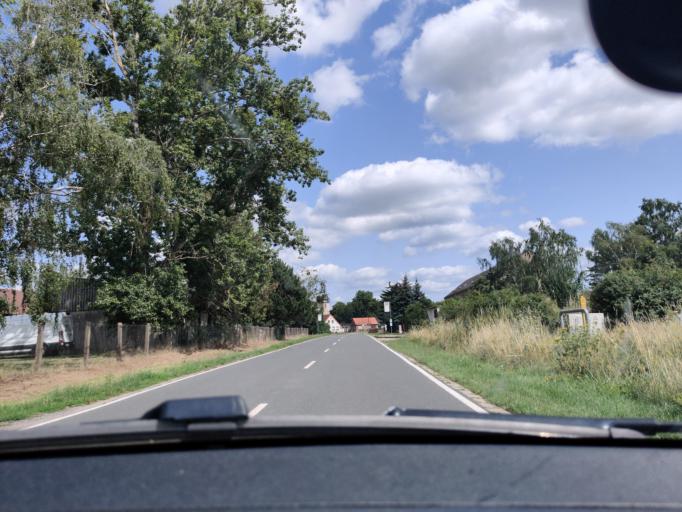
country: DE
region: Saxony-Anhalt
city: Loburg
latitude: 52.0777
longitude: 12.0366
